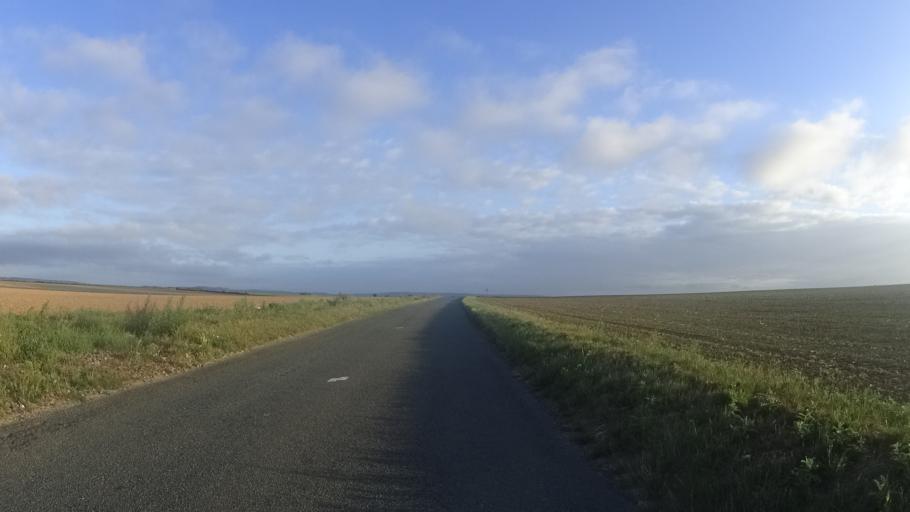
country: FR
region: Picardie
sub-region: Departement de l'Oise
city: Chamant
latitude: 49.1862
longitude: 2.6720
